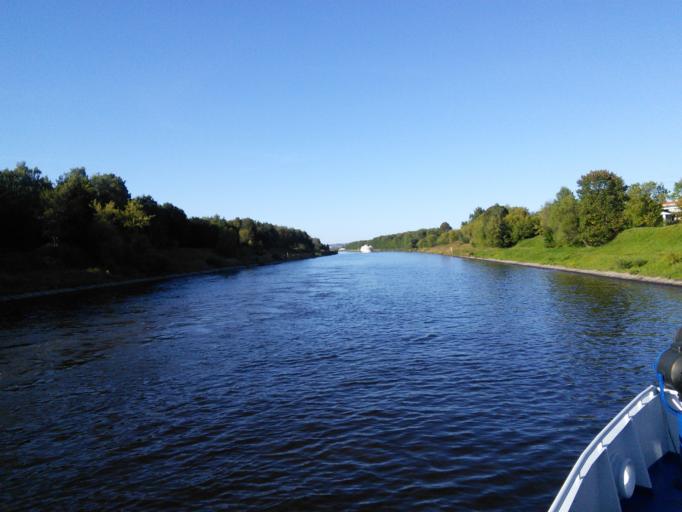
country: RU
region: Moskovskaya
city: Yakhroma
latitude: 56.3242
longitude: 37.4953
